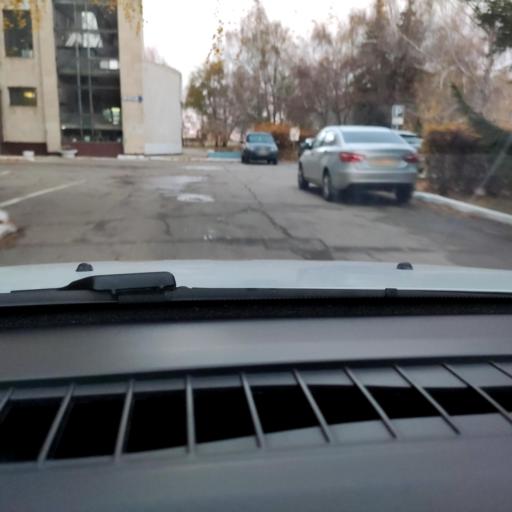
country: RU
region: Samara
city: Tol'yatti
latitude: 53.5516
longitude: 49.2829
